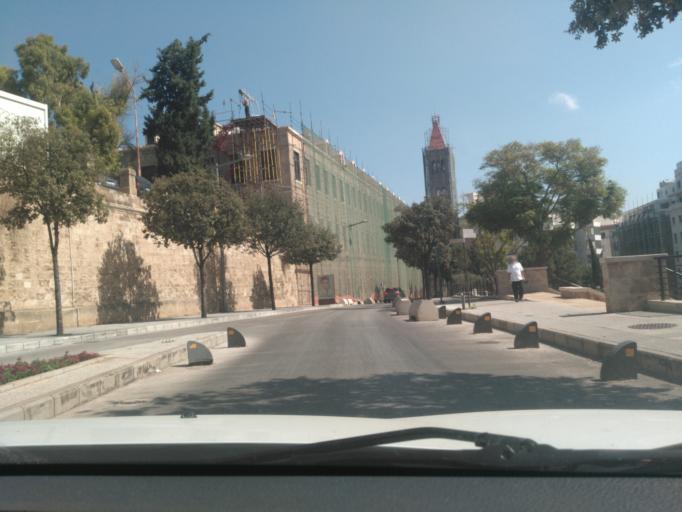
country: LB
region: Beyrouth
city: Beirut
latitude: 33.8967
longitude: 35.5023
